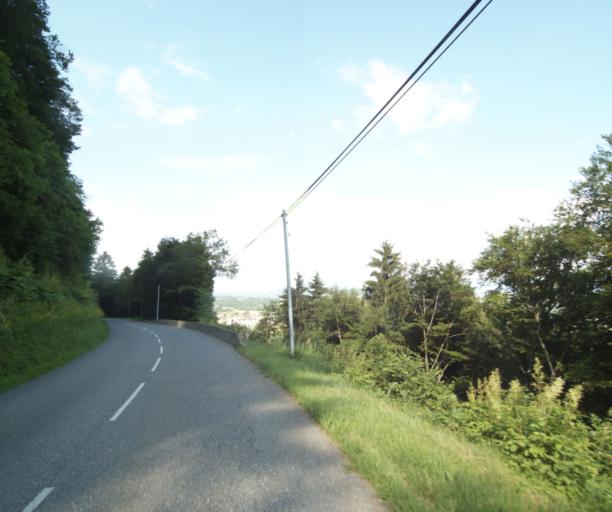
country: FR
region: Rhone-Alpes
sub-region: Departement de la Haute-Savoie
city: Lyaud
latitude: 46.3163
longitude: 6.5018
